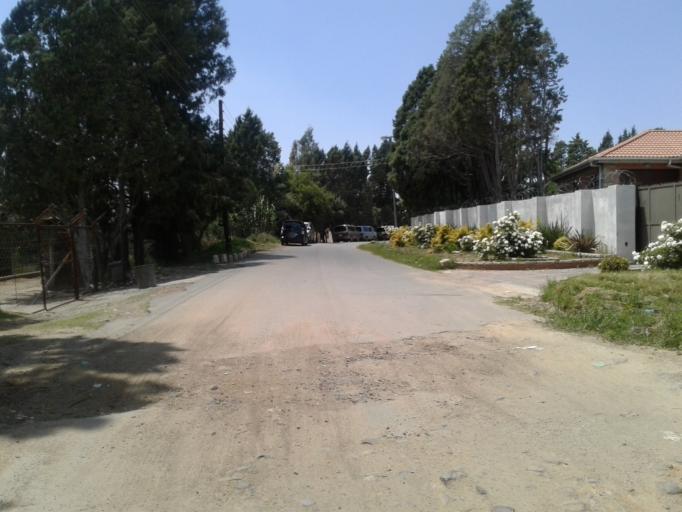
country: LS
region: Maseru
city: Maseru
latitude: -29.3045
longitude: 27.4778
